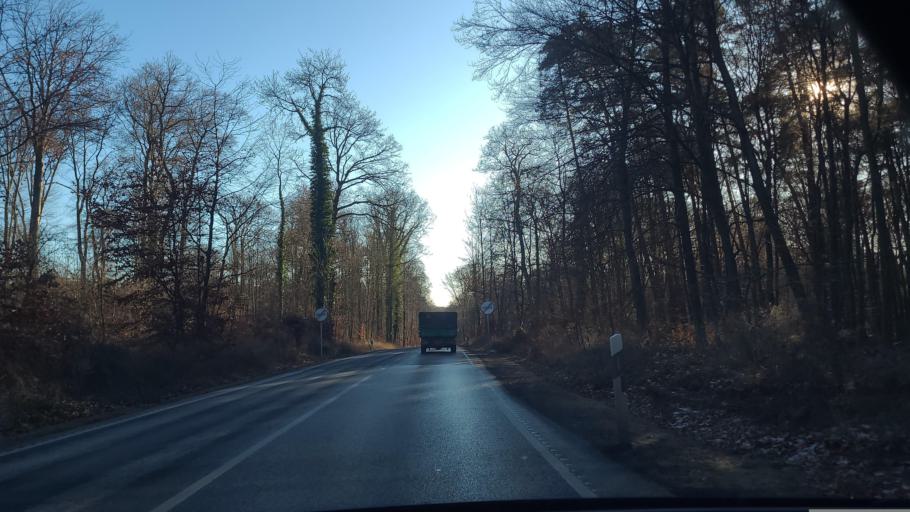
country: LU
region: Luxembourg
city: Bridel
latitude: 49.6452
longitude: 6.0856
